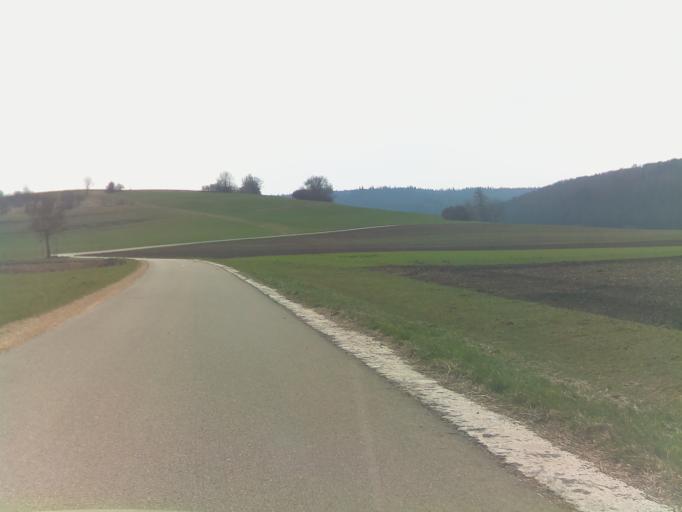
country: DE
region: Baden-Wuerttemberg
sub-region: Tuebingen Region
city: Bad Urach
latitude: 48.4547
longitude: 9.4058
